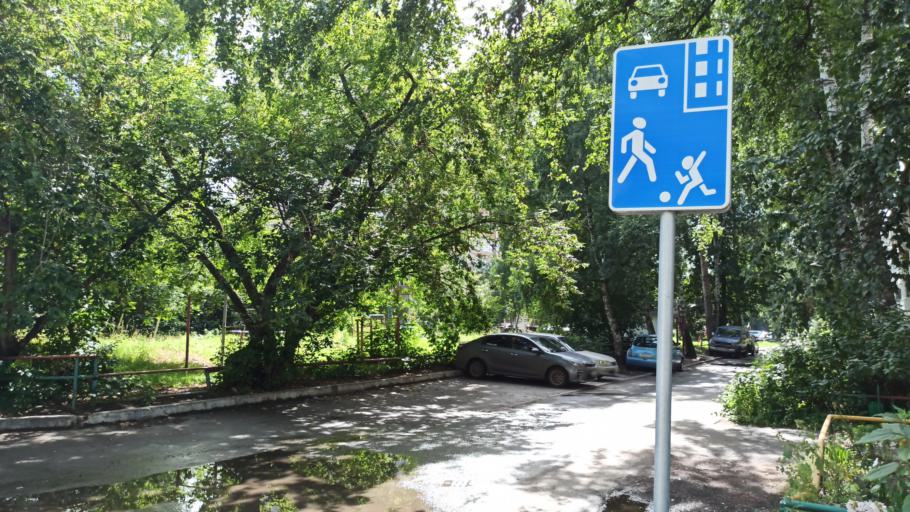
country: RU
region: Tomsk
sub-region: Tomskiy Rayon
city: Tomsk
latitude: 56.4602
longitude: 84.9817
